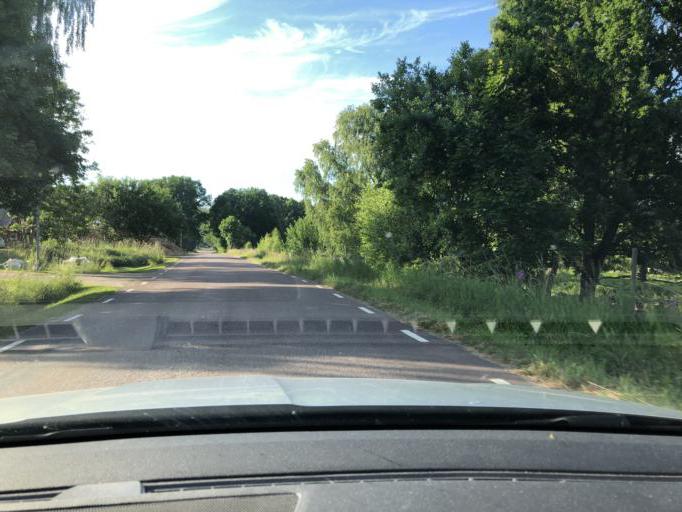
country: SE
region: Blekinge
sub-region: Solvesborgs Kommun
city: Soelvesborg
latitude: 56.1578
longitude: 14.6011
